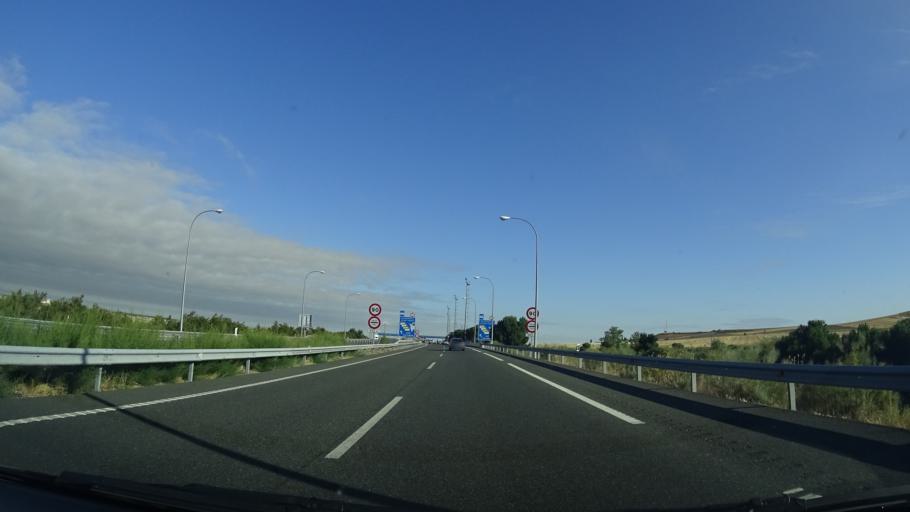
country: ES
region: Castille and Leon
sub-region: Provincia de Avila
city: Sanchidrian
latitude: 40.8792
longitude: -4.5686
